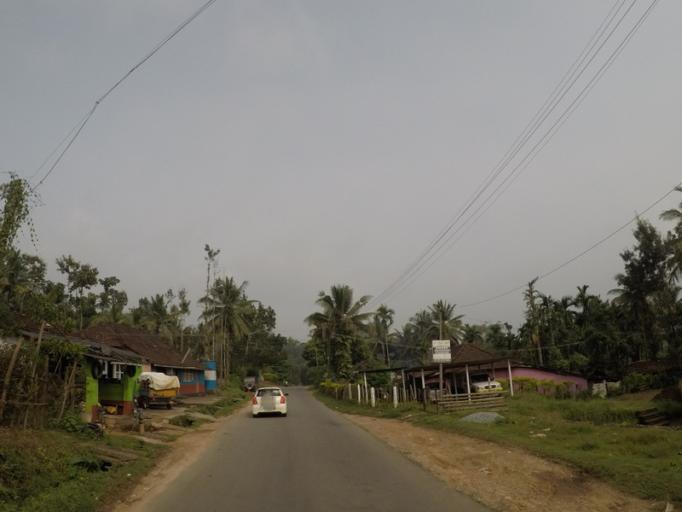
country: IN
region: Karnataka
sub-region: Chikmagalur
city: Chikmagalur
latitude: 13.3409
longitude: 75.5453
